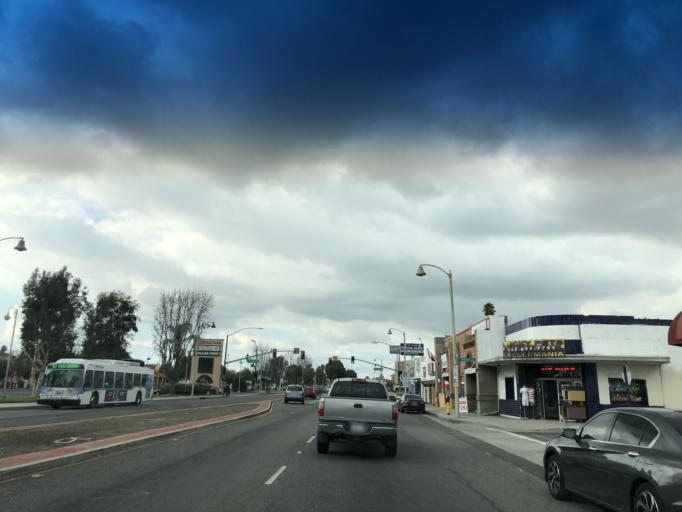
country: US
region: California
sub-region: Los Angeles County
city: Pico Rivera
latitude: 33.9998
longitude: -118.0801
